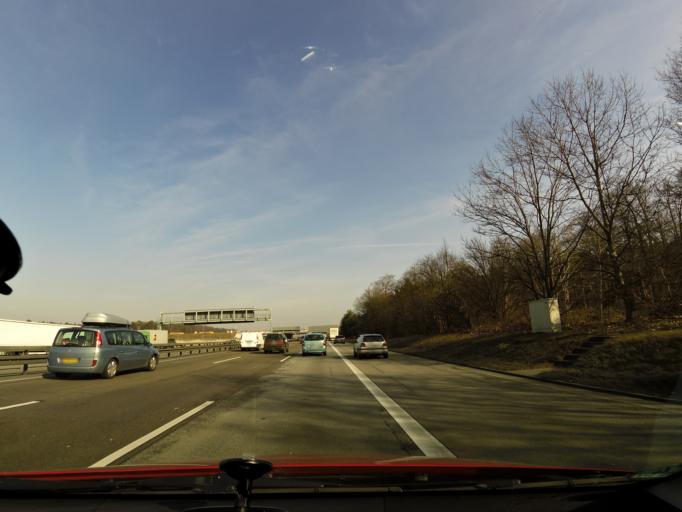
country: DE
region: Hesse
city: Kelsterbach
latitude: 50.0337
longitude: 8.5117
